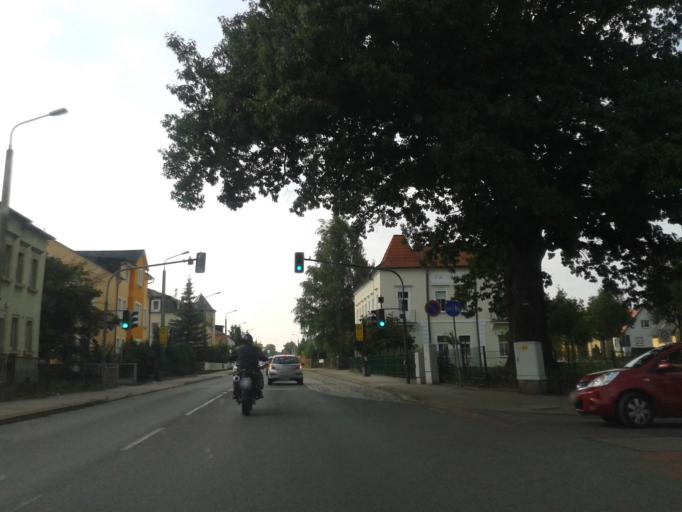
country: DE
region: Saxony
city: Radebeul
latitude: 51.0754
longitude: 13.6667
